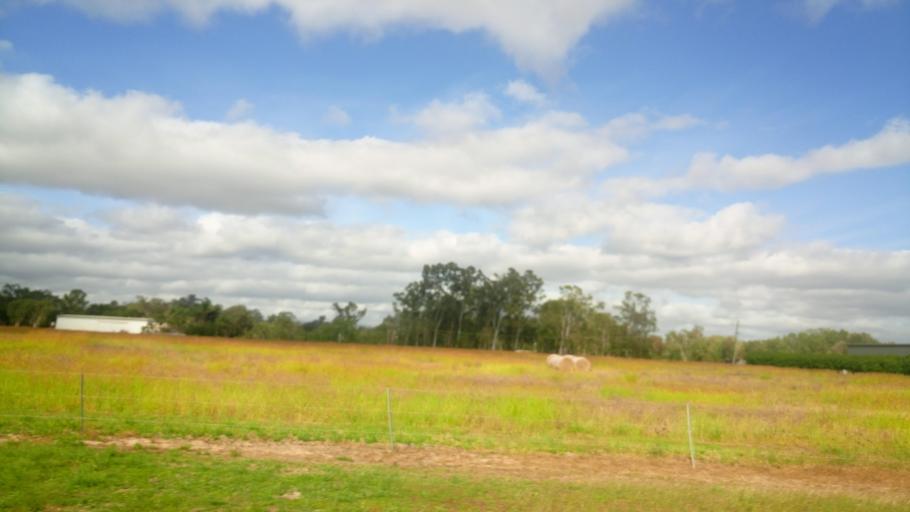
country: AU
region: Queensland
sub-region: Tablelands
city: Mareeba
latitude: -16.9780
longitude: 145.4697
